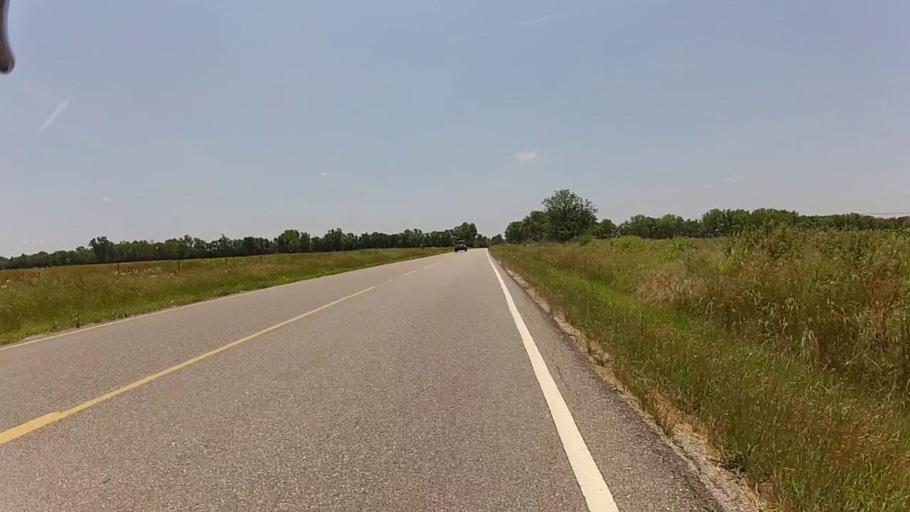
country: US
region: Kansas
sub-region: Montgomery County
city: Cherryvale
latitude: 37.2031
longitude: -95.5389
